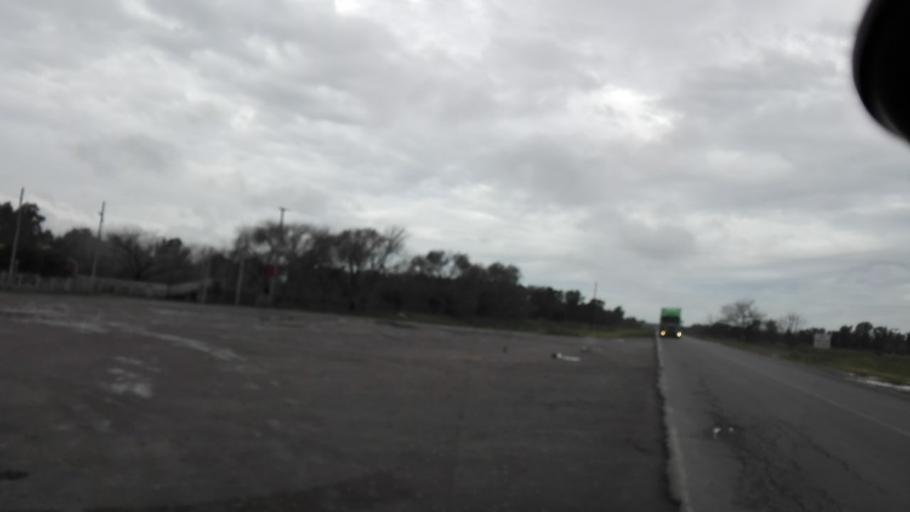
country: AR
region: Buenos Aires
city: San Miguel del Monte
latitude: -35.4398
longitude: -58.7789
